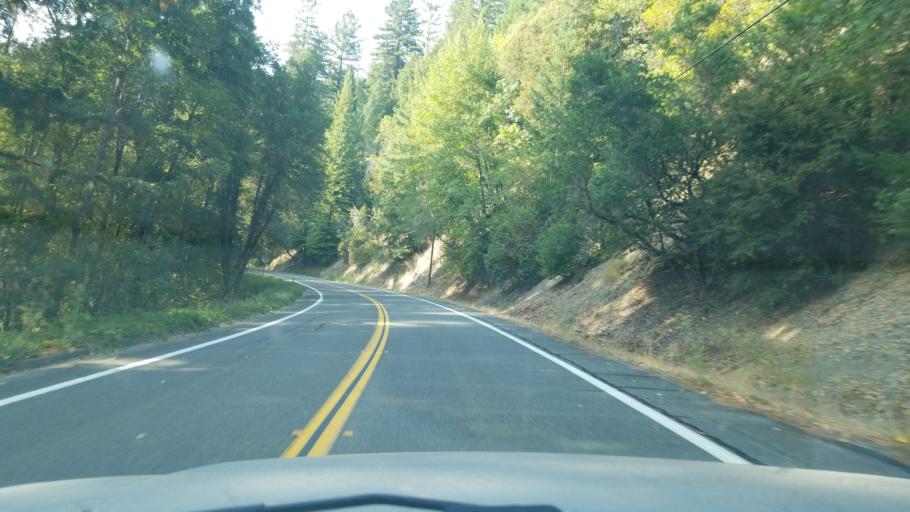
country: US
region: California
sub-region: Humboldt County
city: Redway
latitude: 40.2204
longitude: -123.7863
